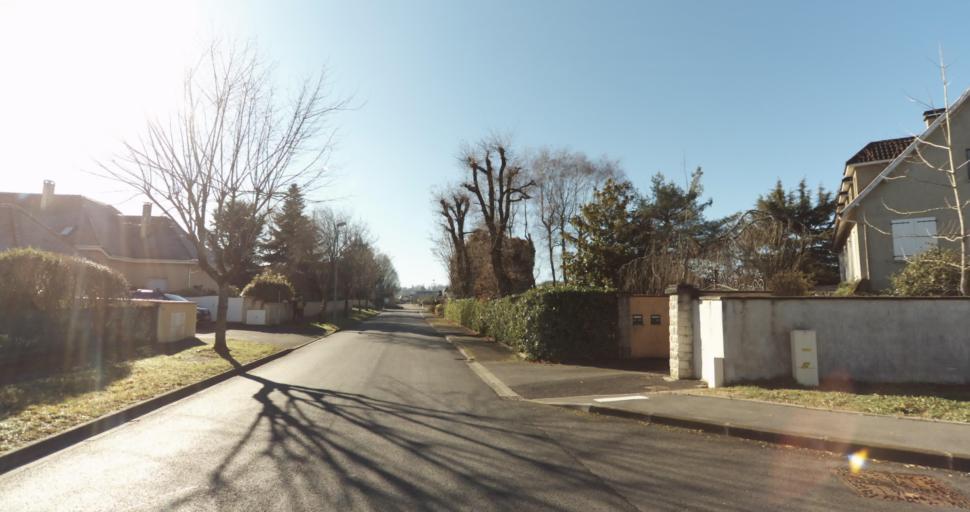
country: FR
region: Aquitaine
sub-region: Departement des Pyrenees-Atlantiques
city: Morlaas
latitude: 43.3530
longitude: -0.2650
